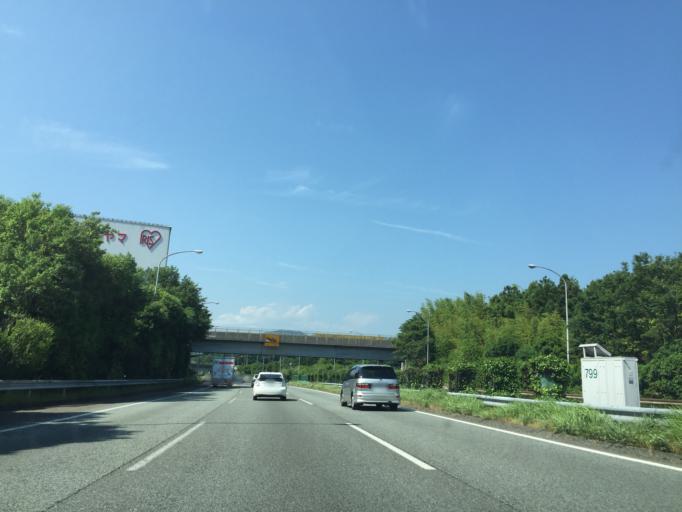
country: JP
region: Shizuoka
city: Gotemba
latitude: 35.3214
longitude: 138.9717
